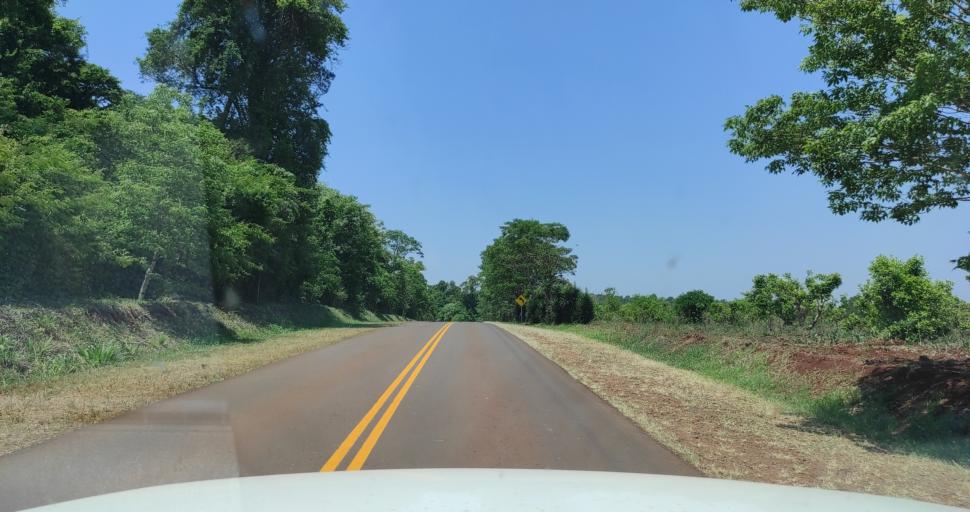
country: AR
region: Misiones
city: Capiovi
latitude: -26.9596
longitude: -55.0916
